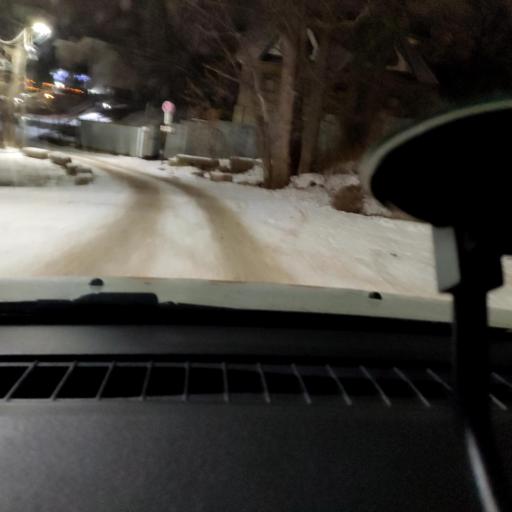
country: RU
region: Samara
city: Samara
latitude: 53.2810
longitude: 50.1890
